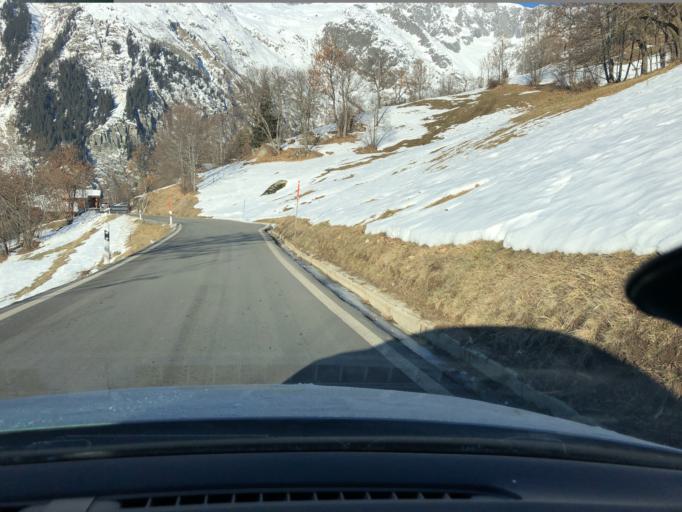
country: CH
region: Valais
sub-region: Goms District
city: Fiesch
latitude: 46.4311
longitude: 8.1519
